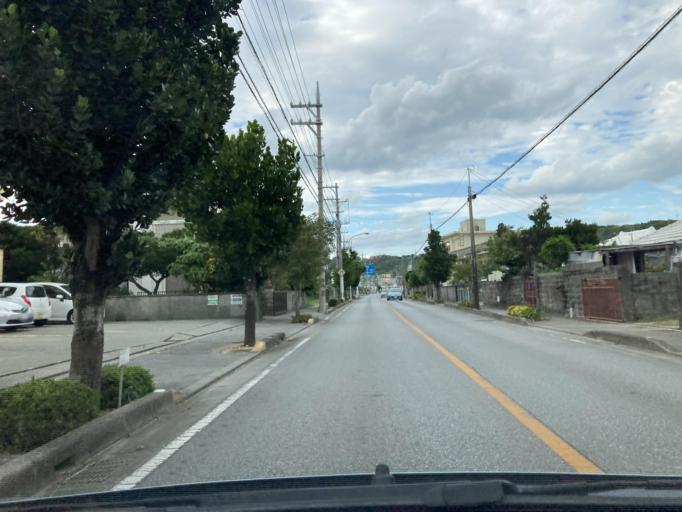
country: JP
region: Okinawa
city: Katsuren-haebaru
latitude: 26.3434
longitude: 127.8686
